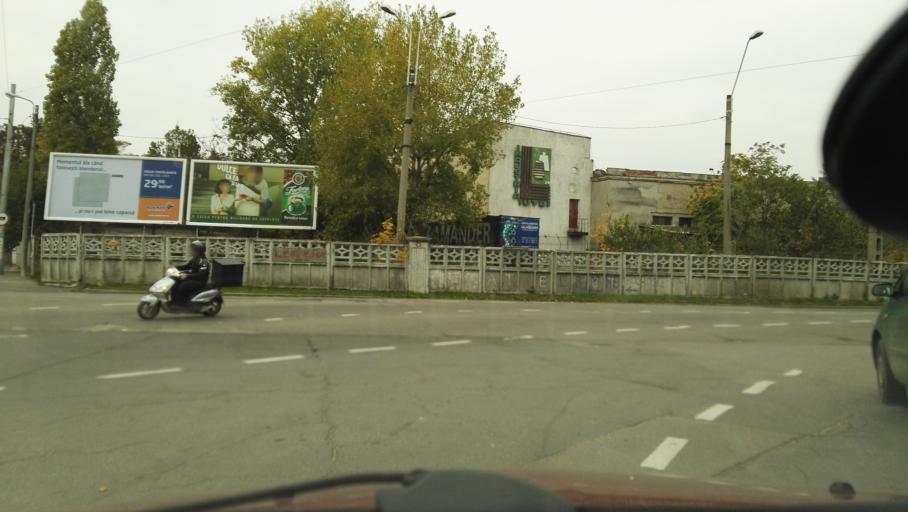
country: RO
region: Bucuresti
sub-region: Municipiul Bucuresti
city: Bucuresti
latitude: 44.4091
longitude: 26.0867
